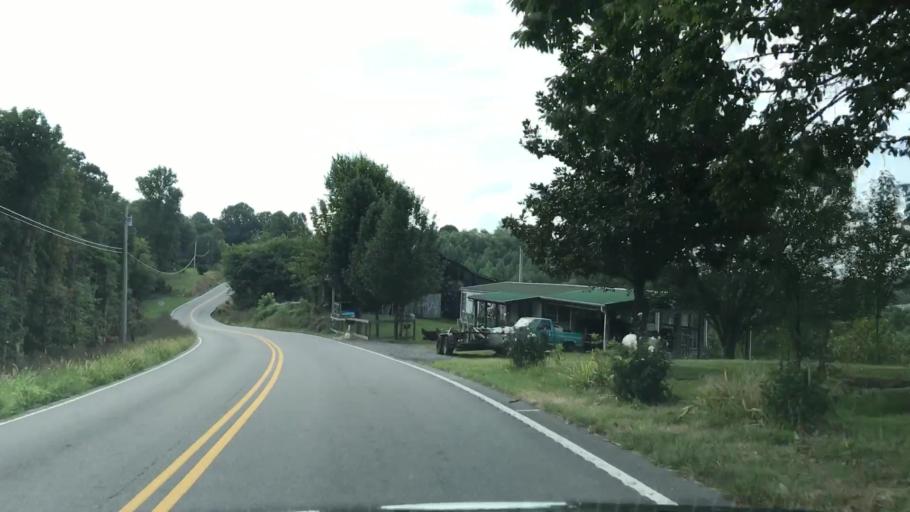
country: US
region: Tennessee
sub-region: Sumner County
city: Westmoreland
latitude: 36.5148
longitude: -86.1794
